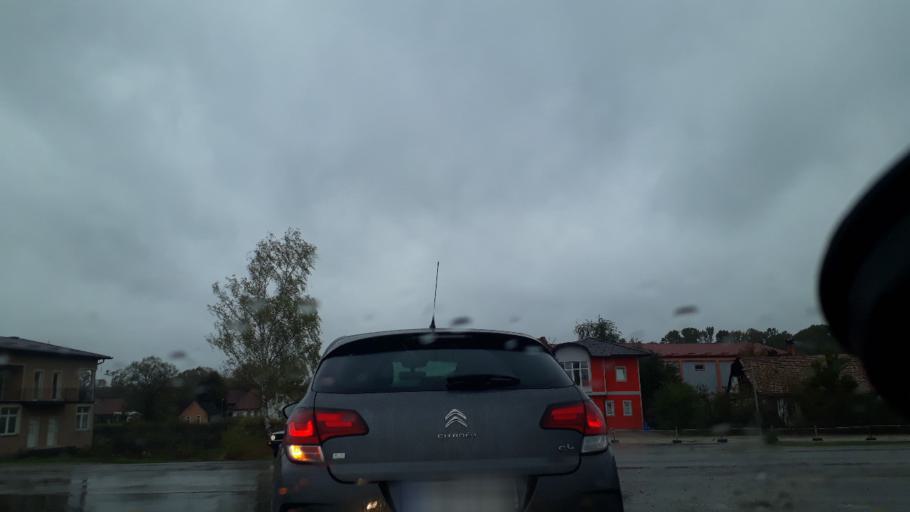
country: BA
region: Republika Srpska
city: Prnjavor
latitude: 44.8558
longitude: 17.6886
